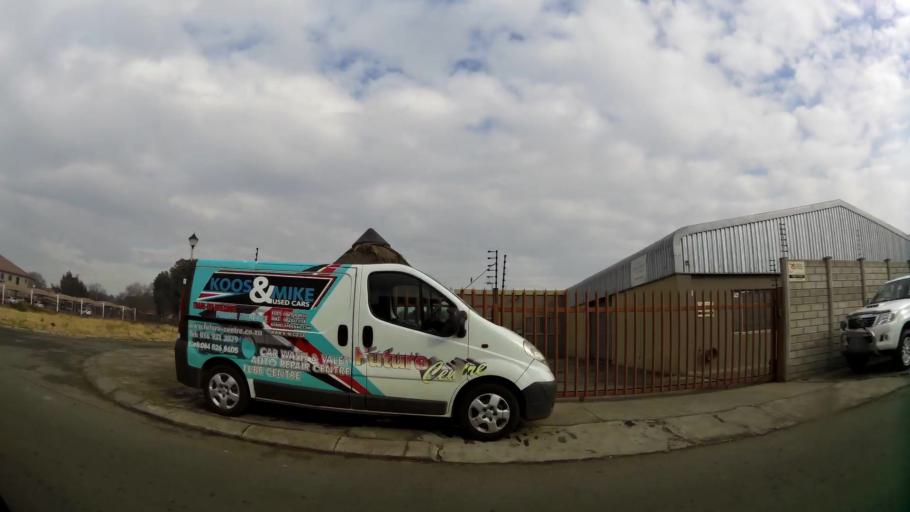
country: ZA
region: Gauteng
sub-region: Sedibeng District Municipality
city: Vanderbijlpark
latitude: -26.6953
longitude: 27.8321
